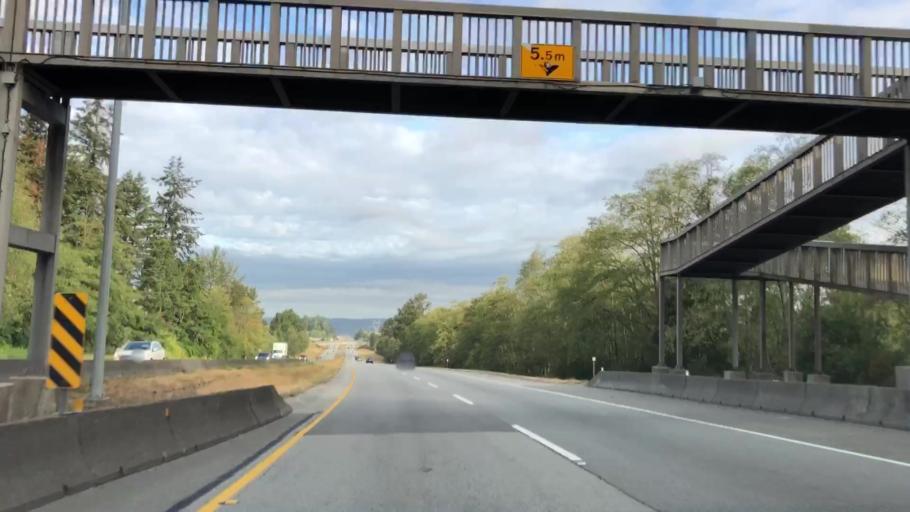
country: CA
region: British Columbia
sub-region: Greater Vancouver Regional District
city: White Rock
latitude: 49.0527
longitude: -122.7932
